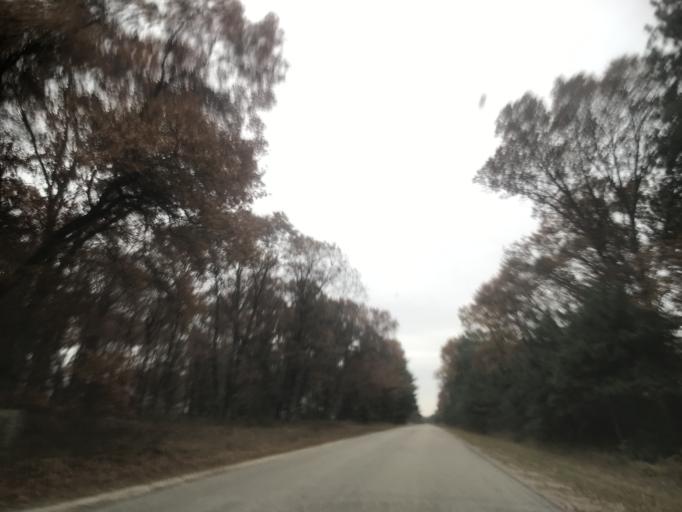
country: US
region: Wisconsin
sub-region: Oconto County
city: Gillett
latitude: 45.3091
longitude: -88.2713
